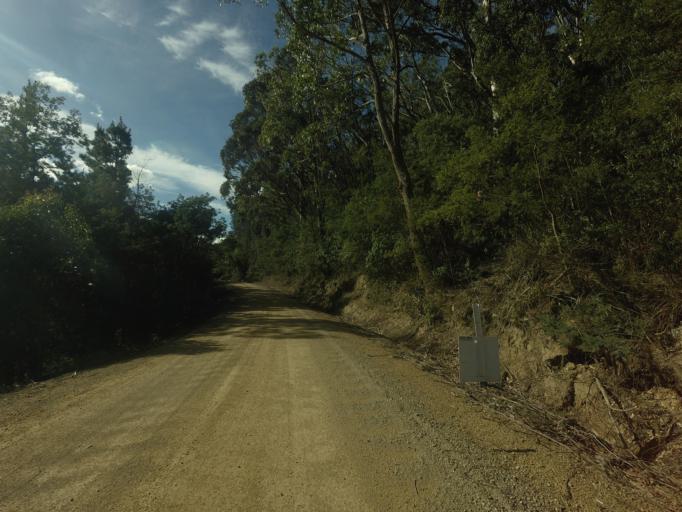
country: AU
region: Tasmania
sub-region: Clarence
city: Sandford
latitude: -43.1797
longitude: 147.7712
